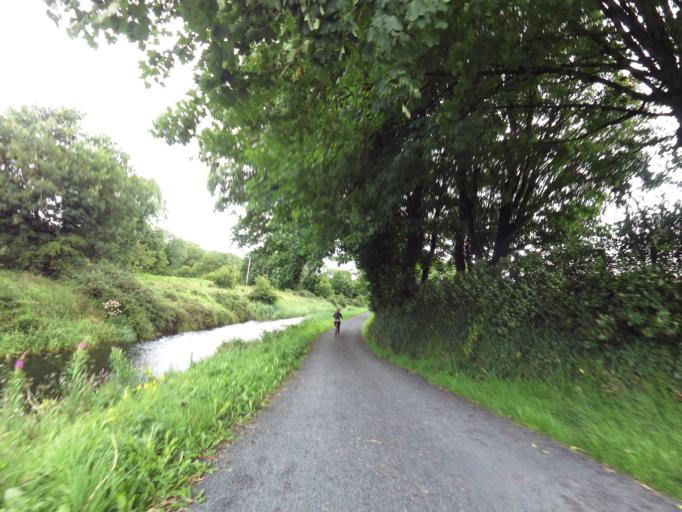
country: IE
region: Leinster
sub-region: An Iarmhi
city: An Muileann gCearr
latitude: 53.5278
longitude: -7.4519
